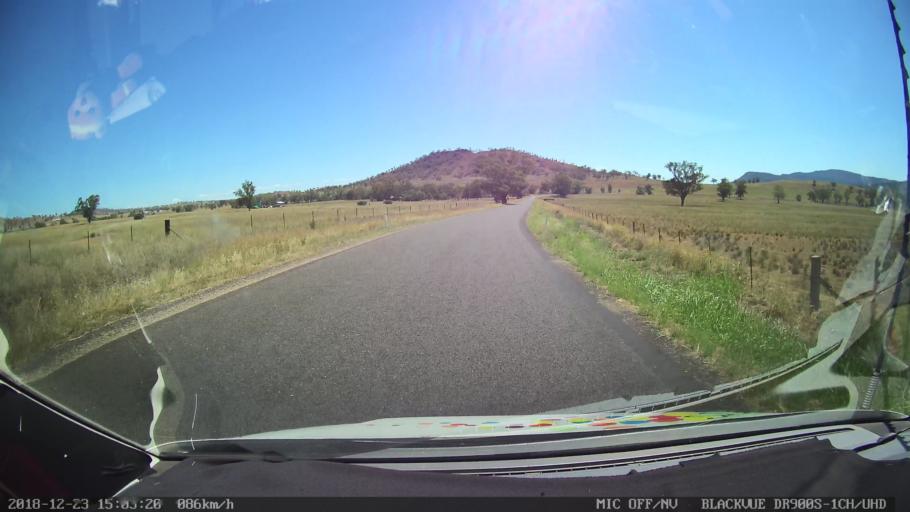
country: AU
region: New South Wales
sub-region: Tamworth Municipality
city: Manilla
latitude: -30.7376
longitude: 150.7661
